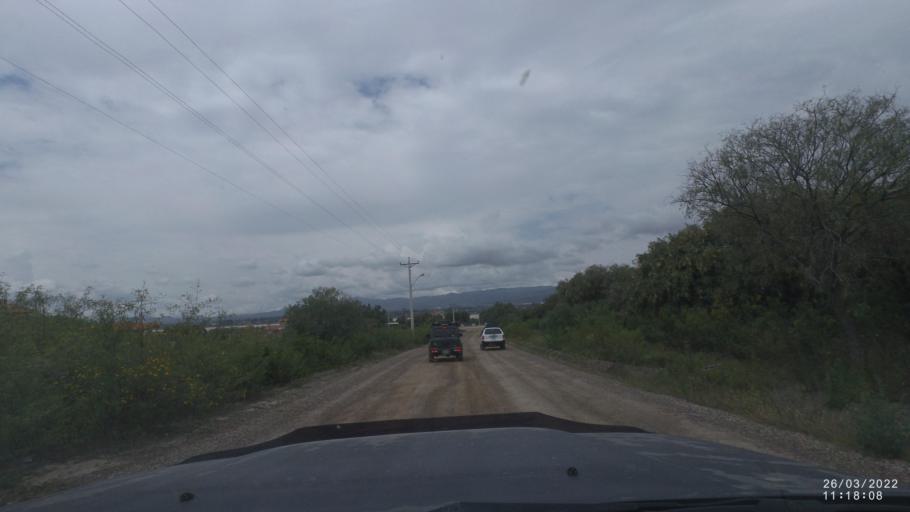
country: BO
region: Cochabamba
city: Tarata
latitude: -17.5425
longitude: -66.0225
